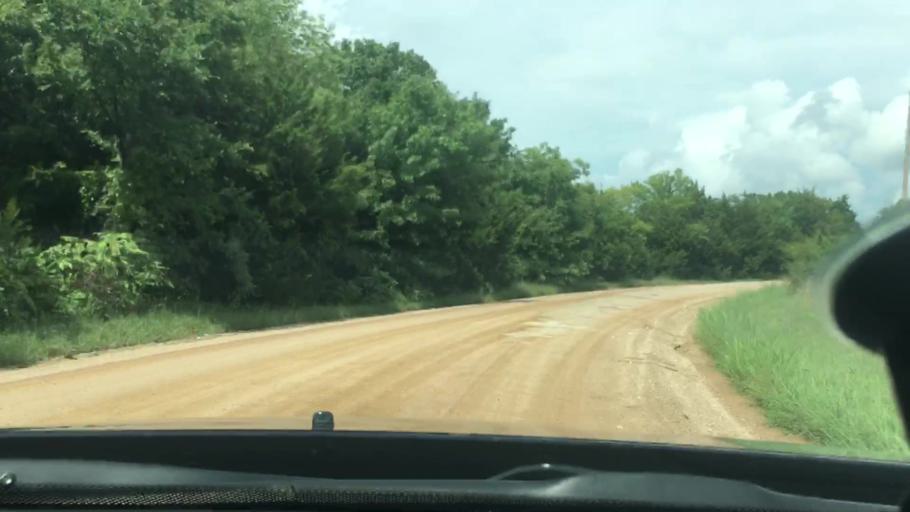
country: US
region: Oklahoma
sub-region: Carter County
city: Dickson
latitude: 34.2455
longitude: -96.9281
